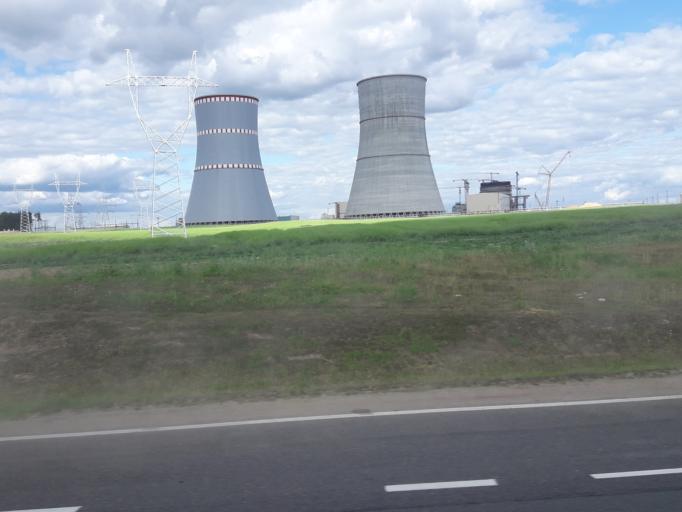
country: BY
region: Grodnenskaya
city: Astravyets
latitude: 54.7568
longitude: 26.0734
